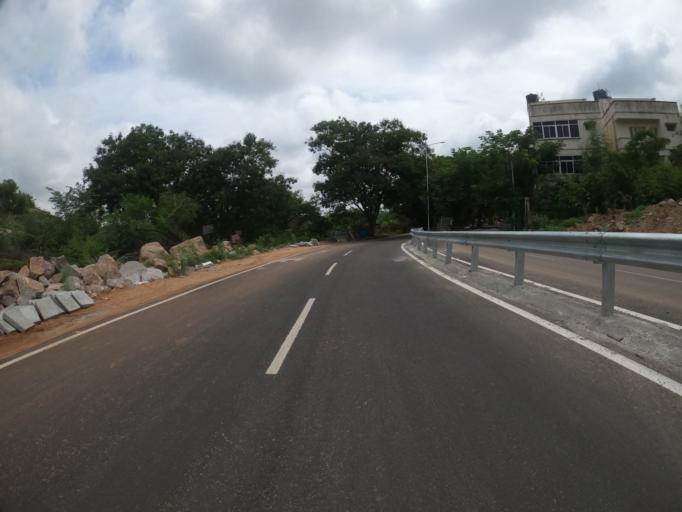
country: IN
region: Telangana
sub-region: Rangareddi
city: Kukatpalli
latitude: 17.4222
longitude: 78.3981
